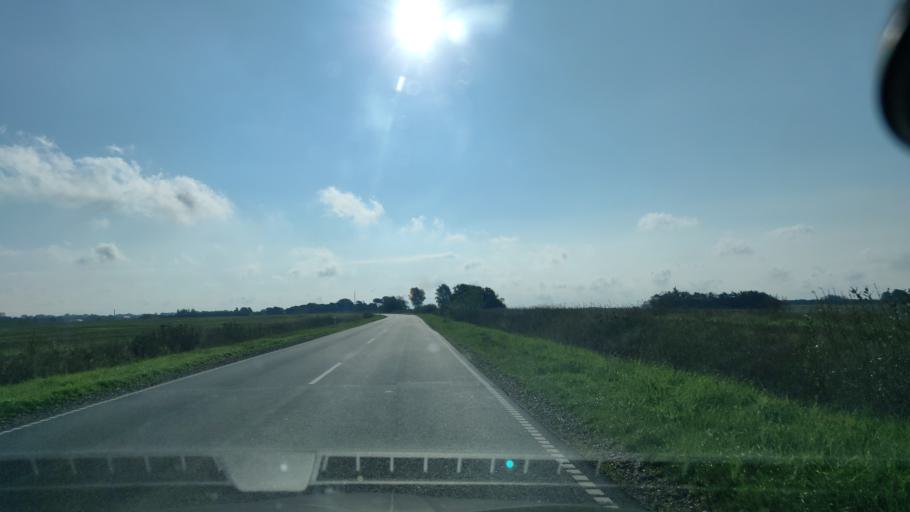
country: DK
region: North Denmark
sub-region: Hjorring Kommune
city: Vra
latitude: 57.3543
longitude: 9.8953
